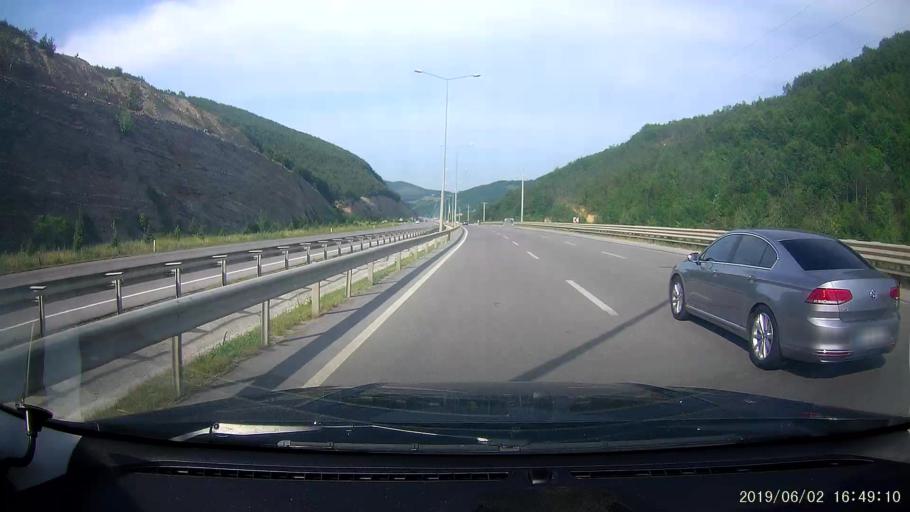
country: TR
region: Samsun
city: Taflan
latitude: 41.2337
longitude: 36.1554
